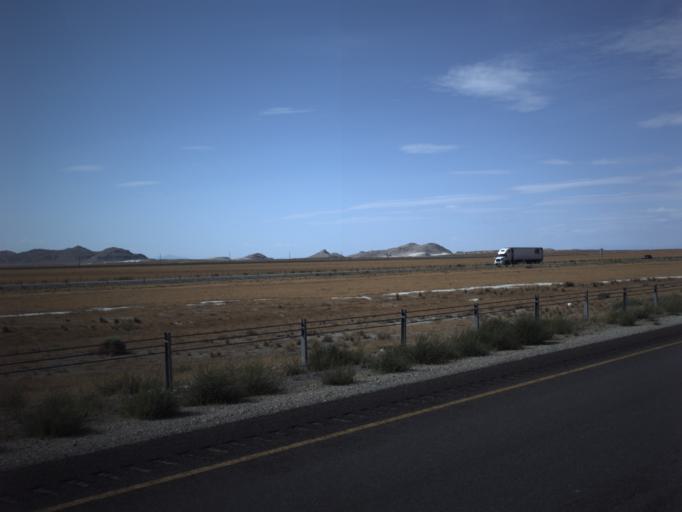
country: US
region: Utah
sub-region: Tooele County
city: Grantsville
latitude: 40.7271
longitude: -113.2394
